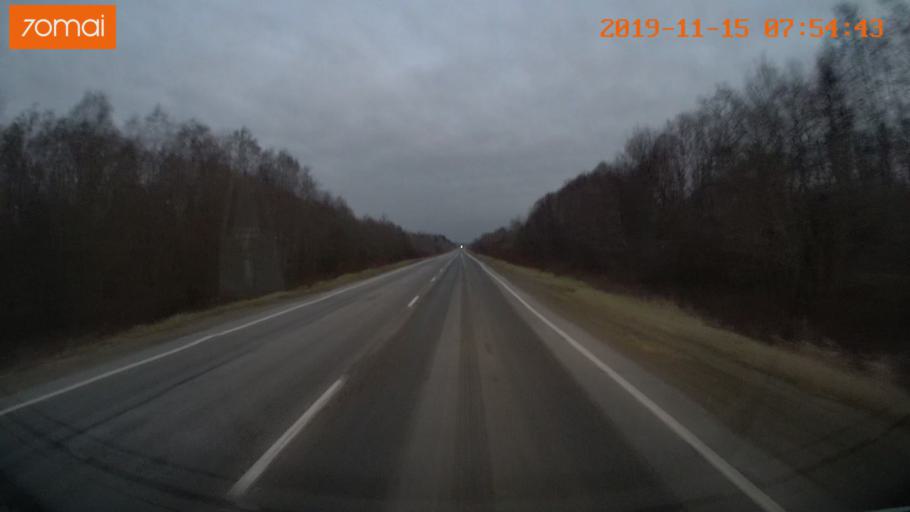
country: RU
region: Vologda
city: Cherepovets
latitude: 58.9015
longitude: 38.1724
